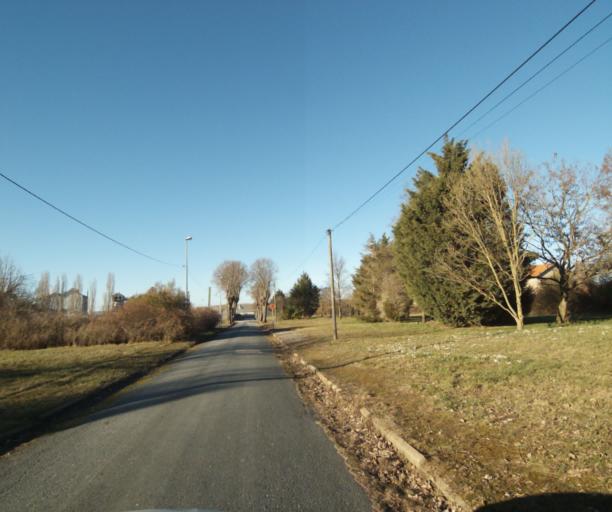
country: FR
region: Lorraine
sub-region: Departement de Meurthe-et-Moselle
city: Art-sur-Meurthe
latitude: 48.6368
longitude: 6.2689
